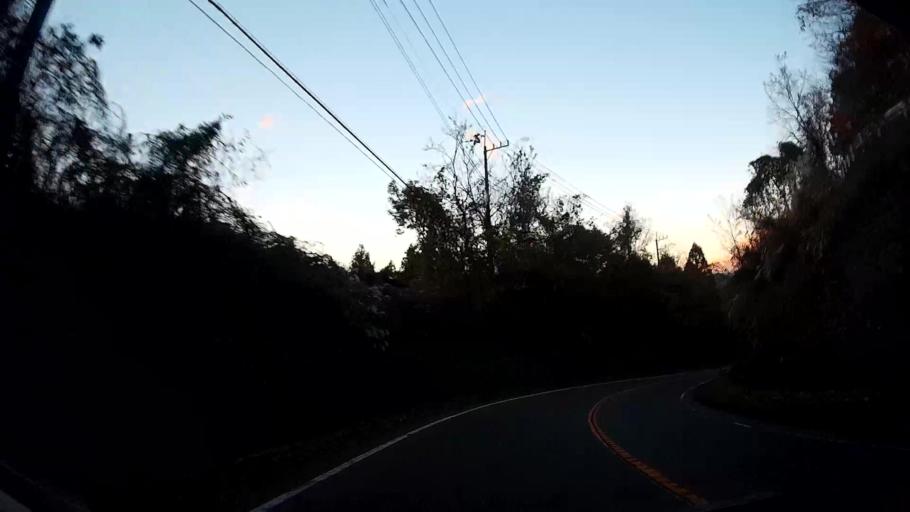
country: JP
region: Yamanashi
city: Uenohara
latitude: 35.5769
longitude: 139.2246
